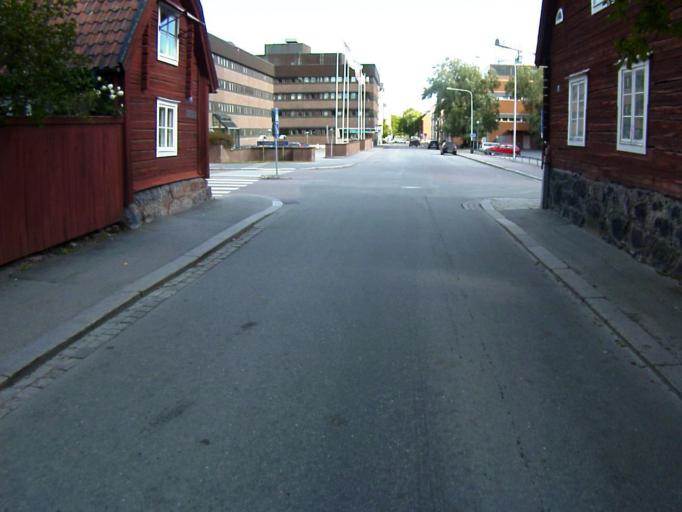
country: SE
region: Soedermanland
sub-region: Eskilstuna Kommun
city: Eskilstuna
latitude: 59.3705
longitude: 16.5048
